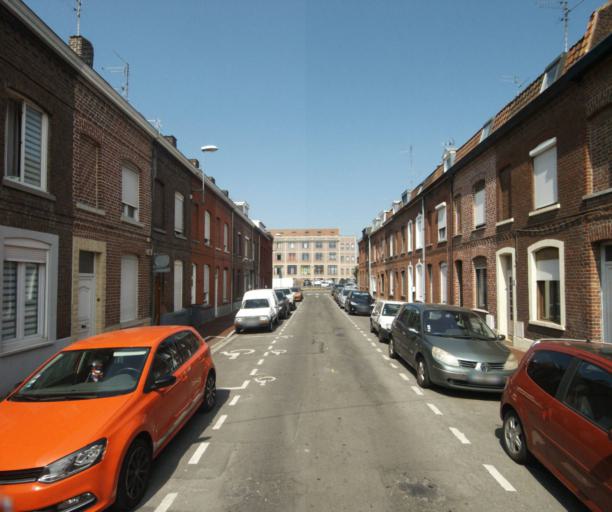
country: FR
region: Nord-Pas-de-Calais
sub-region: Departement du Nord
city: Tourcoing
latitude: 50.7317
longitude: 3.1667
